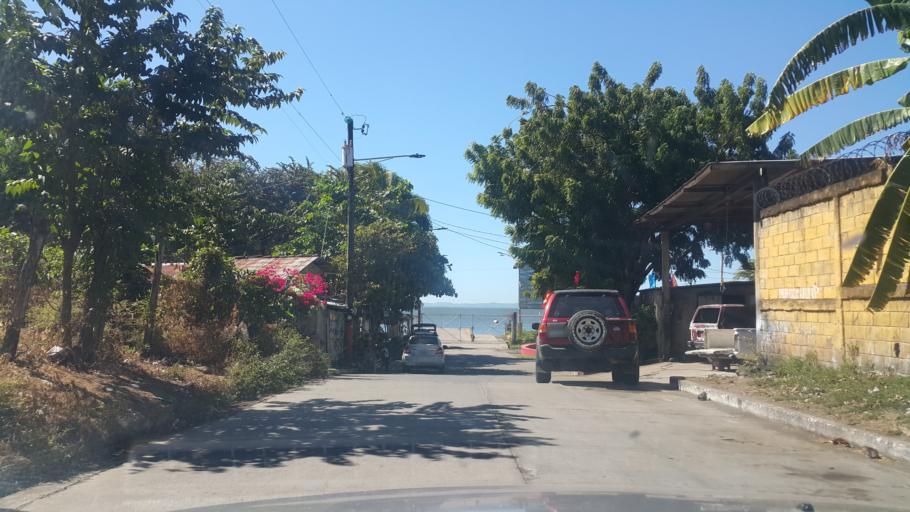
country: NI
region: Rivas
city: Moyogalpa
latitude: 11.5397
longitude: -85.7005
